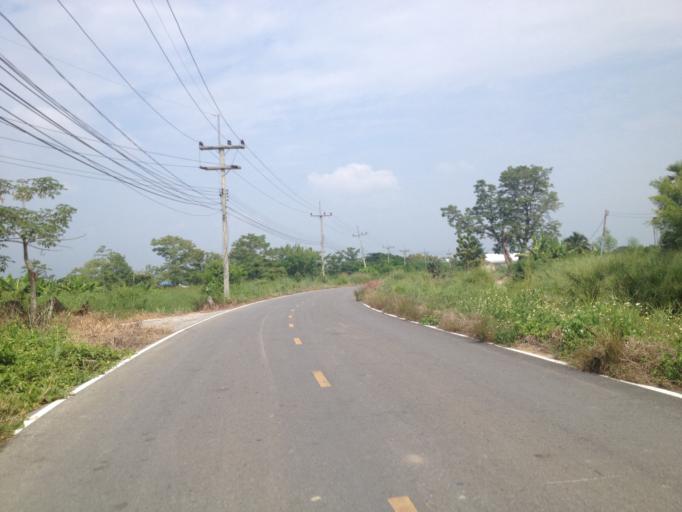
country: TH
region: Chiang Mai
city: San Pa Tong
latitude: 18.6551
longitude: 98.8716
